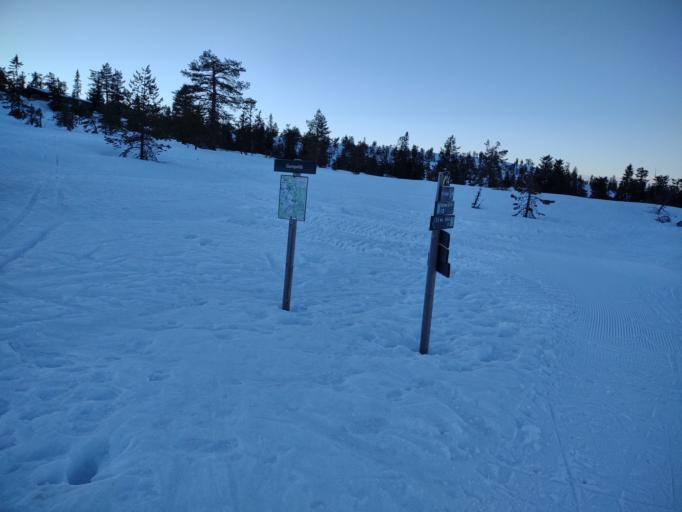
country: NO
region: Buskerud
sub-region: Flesberg
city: Lampeland
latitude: 59.7608
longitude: 9.4402
